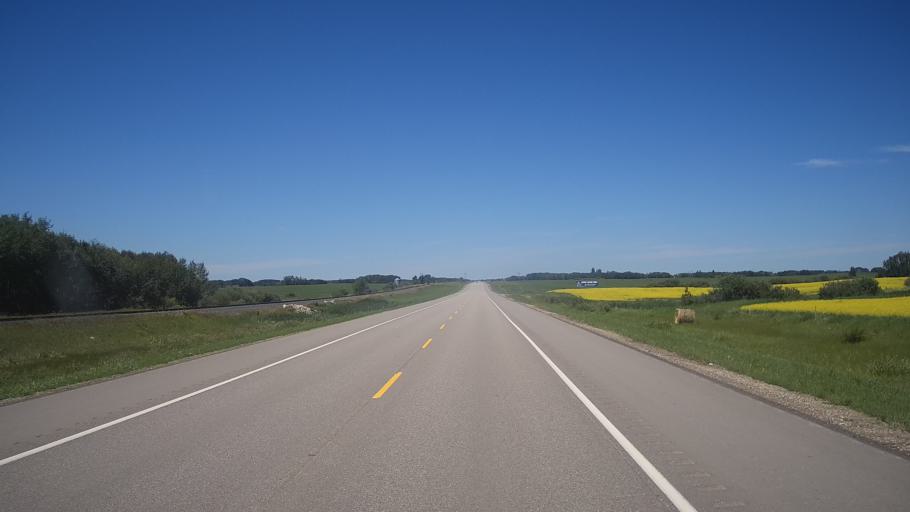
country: CA
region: Manitoba
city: Minnedosa
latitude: 50.2722
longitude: -99.9390
